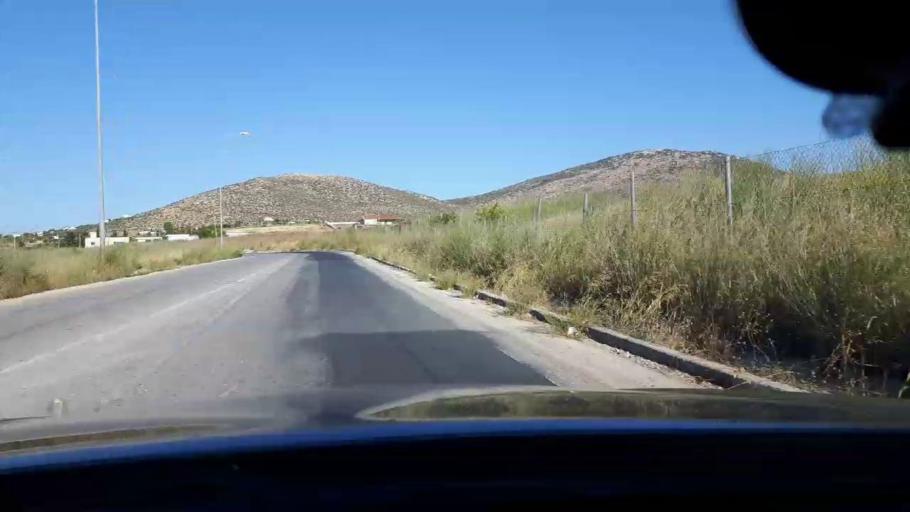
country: GR
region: Attica
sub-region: Nomarchia Anatolikis Attikis
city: Limin Mesoyaias
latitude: 37.8866
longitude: 23.9733
